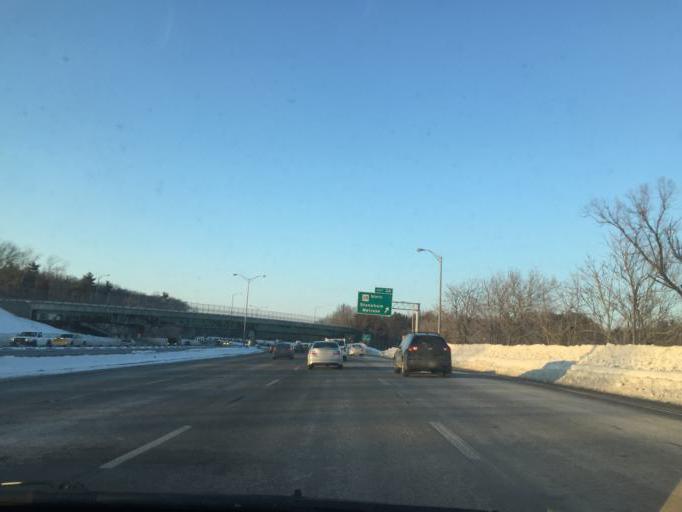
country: US
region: Massachusetts
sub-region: Middlesex County
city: Stoneham
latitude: 42.4576
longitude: -71.1020
